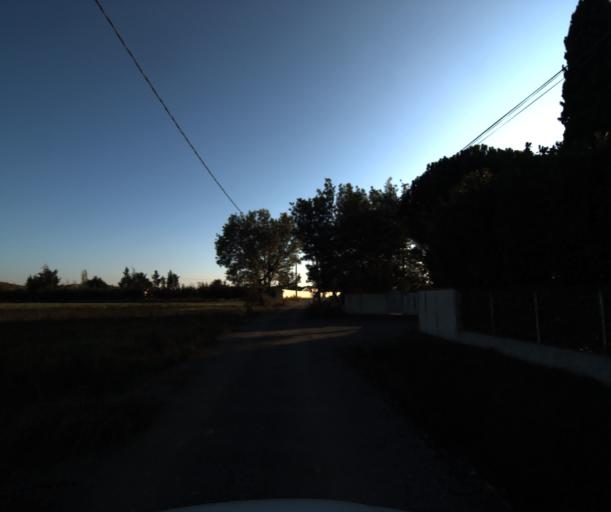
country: FR
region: Midi-Pyrenees
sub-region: Departement de la Haute-Garonne
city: Colomiers
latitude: 43.6253
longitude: 1.3393
